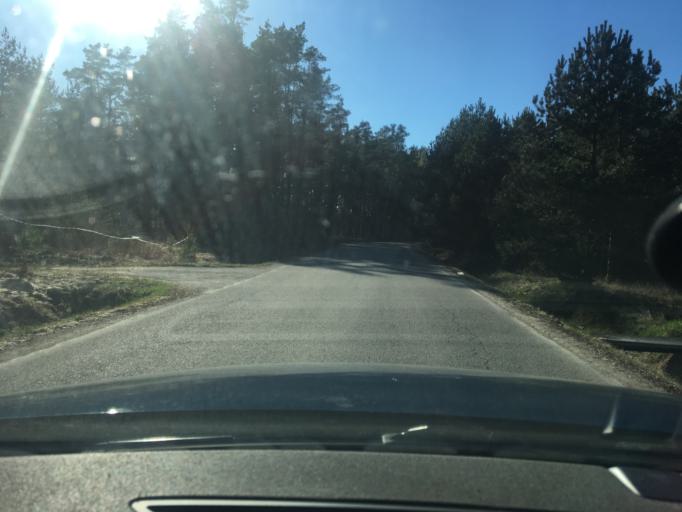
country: LV
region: Salaspils
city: Salaspils
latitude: 56.8666
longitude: 24.3110
